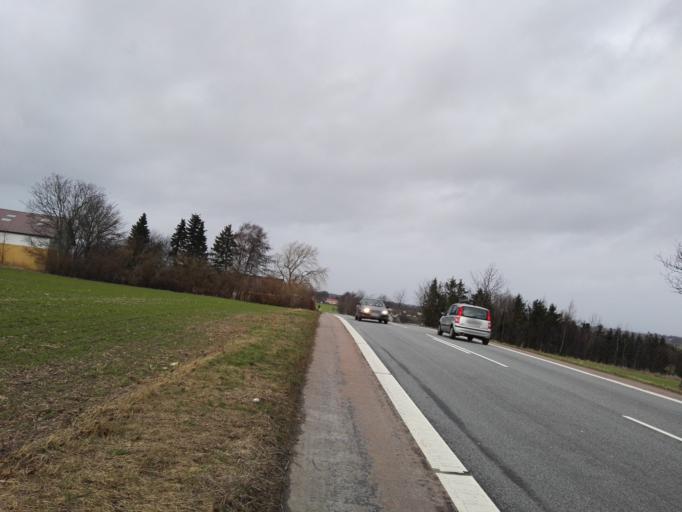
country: DK
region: Capital Region
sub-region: Frederikssund Kommune
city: Skibby
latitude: 55.6785
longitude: 11.9289
